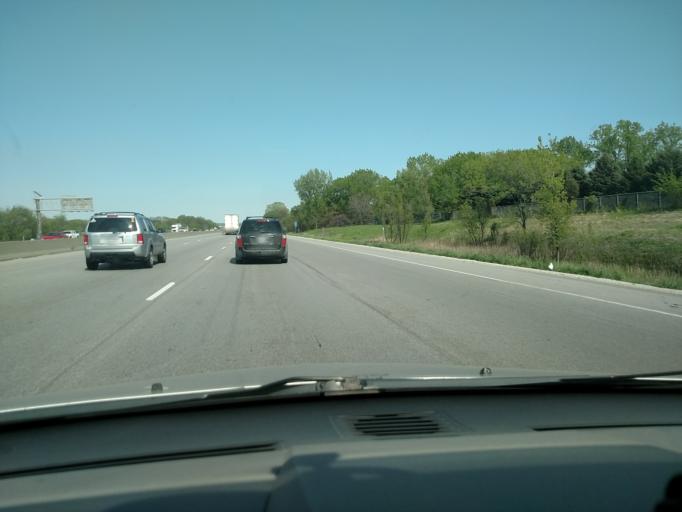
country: US
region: Iowa
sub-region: Polk County
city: Urbandale
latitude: 41.6522
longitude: -93.7300
